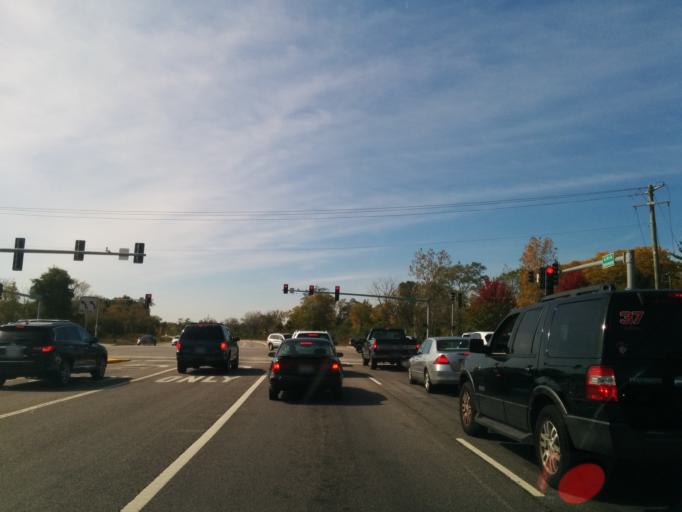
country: US
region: Illinois
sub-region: DuPage County
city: Warrenville
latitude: 41.8303
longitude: -88.1675
